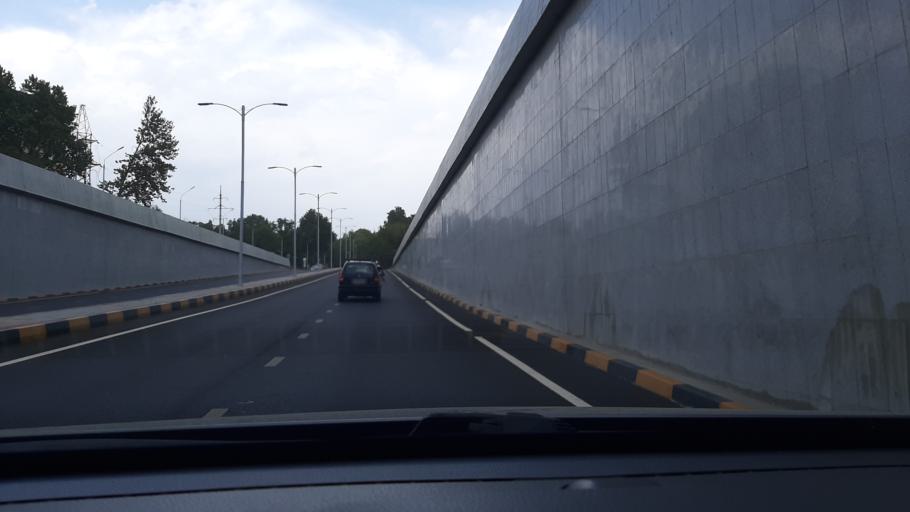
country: TJ
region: Dushanbe
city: Dushanbe
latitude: 38.5853
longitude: 68.7554
